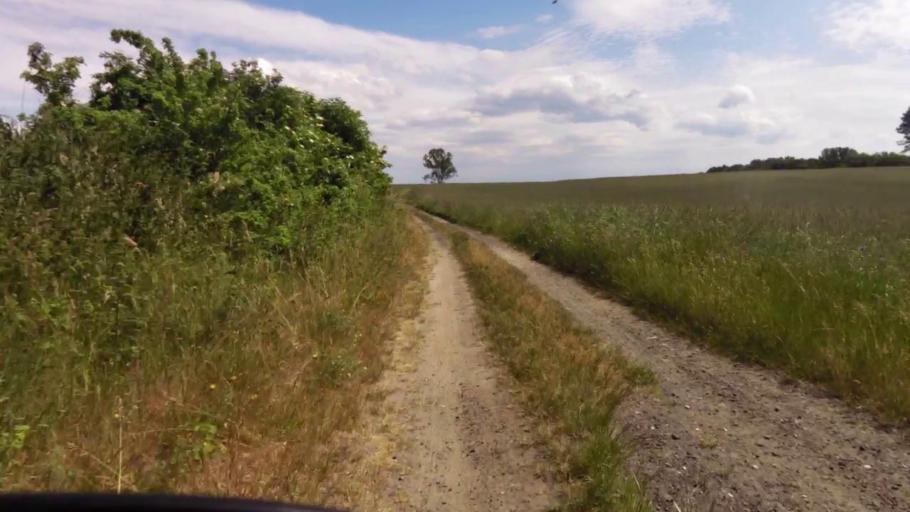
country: PL
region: West Pomeranian Voivodeship
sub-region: Powiat kamienski
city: Wolin
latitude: 53.8578
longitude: 14.5599
